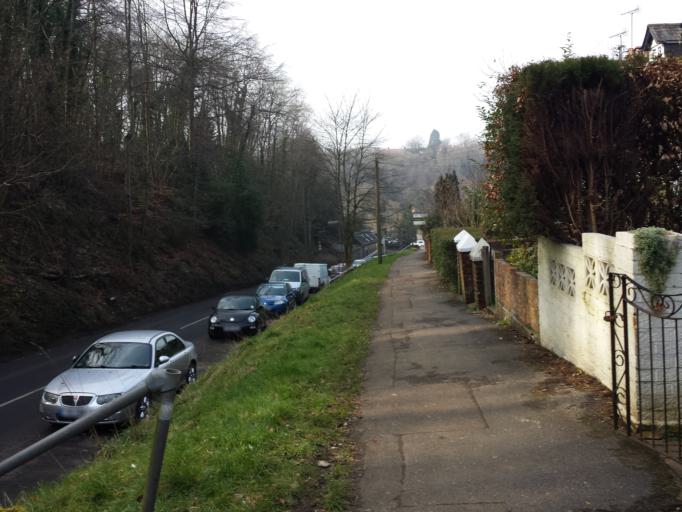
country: GB
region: England
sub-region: Surrey
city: Godalming
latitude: 51.1797
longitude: -0.6209
